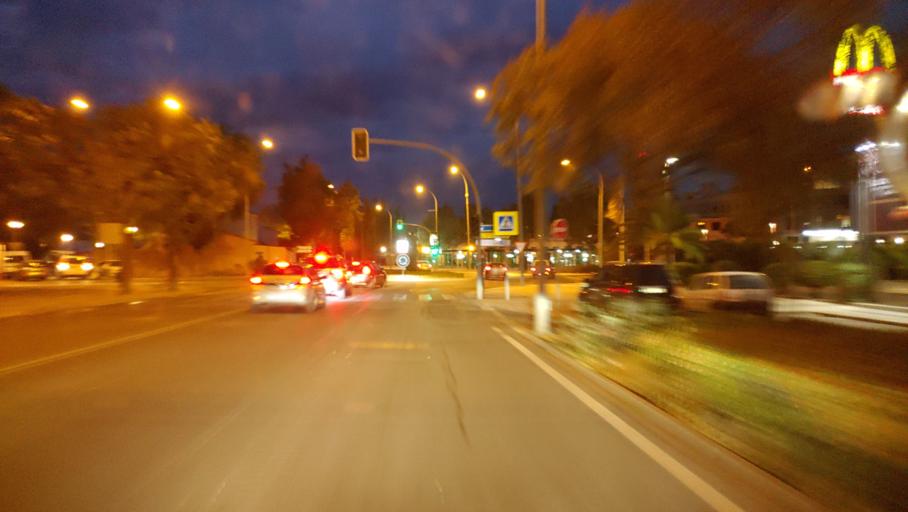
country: ES
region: Castille-La Mancha
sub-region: Provincia de Ciudad Real
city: Ciudad Real
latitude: 38.9840
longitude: -3.9147
